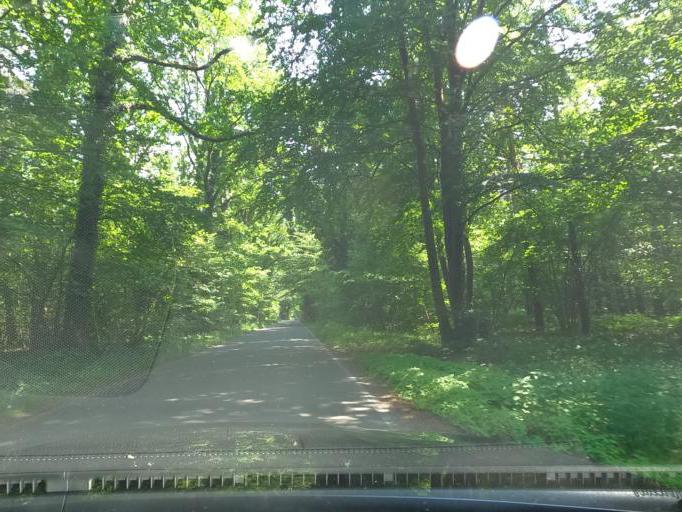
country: DE
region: Lower Saxony
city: Isernhagen Farster Bauerschaft
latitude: 52.4070
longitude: 9.8530
